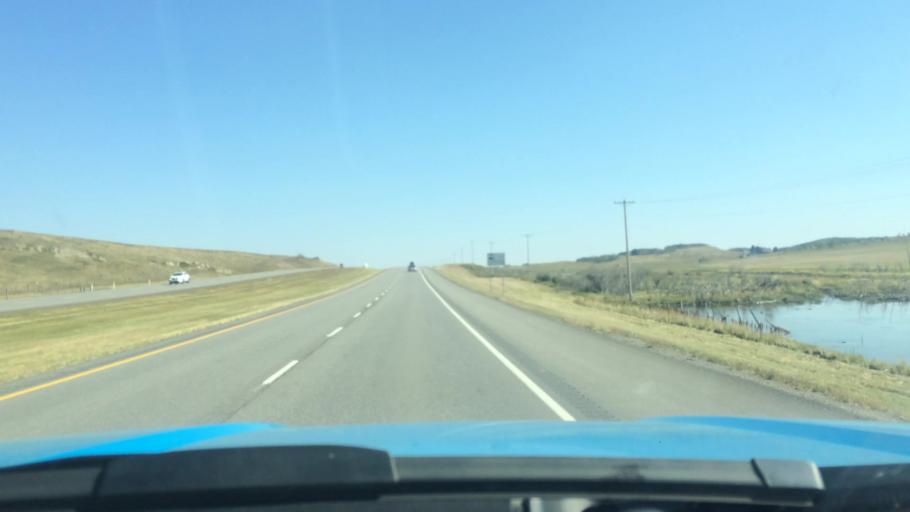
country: CA
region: Alberta
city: Cochrane
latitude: 51.1181
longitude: -114.6619
